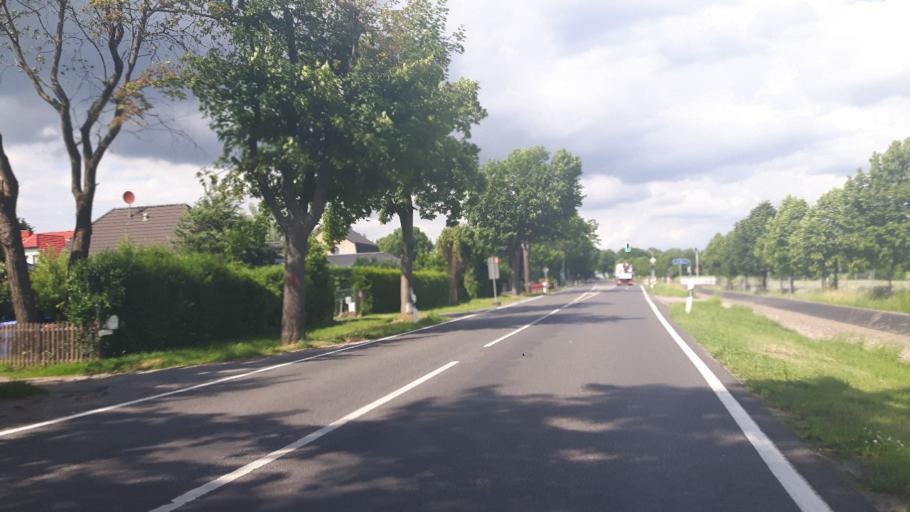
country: DE
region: Brandenburg
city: Bernau bei Berlin
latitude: 52.6434
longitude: 13.5638
